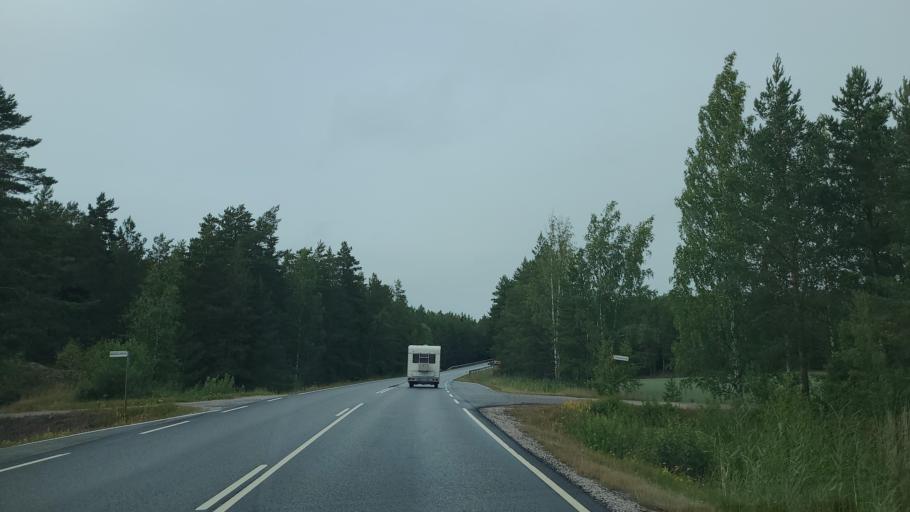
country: FI
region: Varsinais-Suomi
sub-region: Turku
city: Sauvo
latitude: 60.2774
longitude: 22.6683
